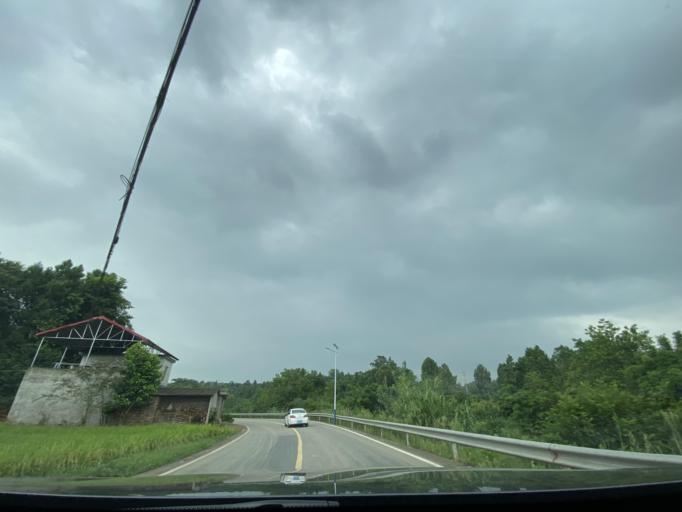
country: CN
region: Sichuan
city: Jiancheng
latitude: 30.5487
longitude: 104.5234
